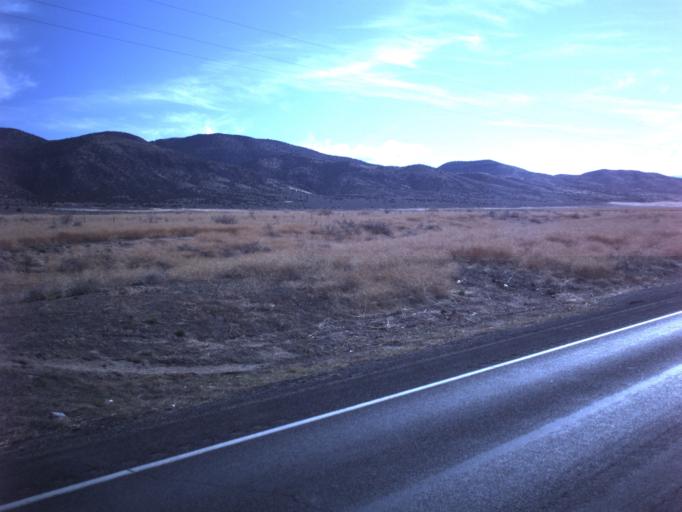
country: US
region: Utah
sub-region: Sanpete County
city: Gunnison
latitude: 39.2710
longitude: -111.8725
